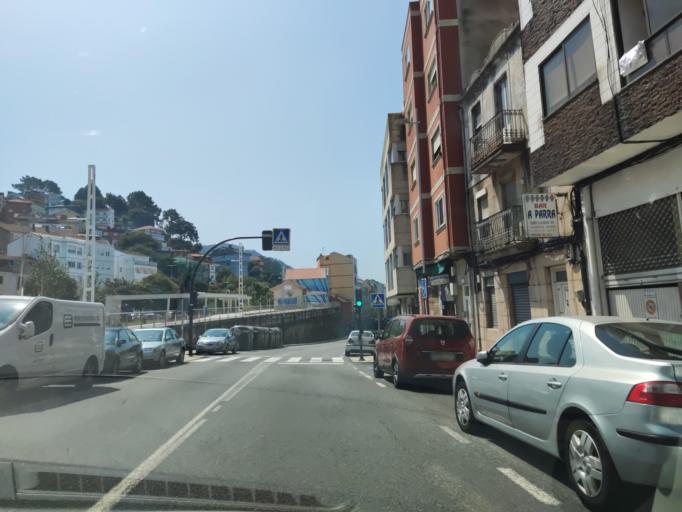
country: ES
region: Galicia
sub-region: Provincia de Pontevedra
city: Redondela
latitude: 42.2691
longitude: -8.6704
